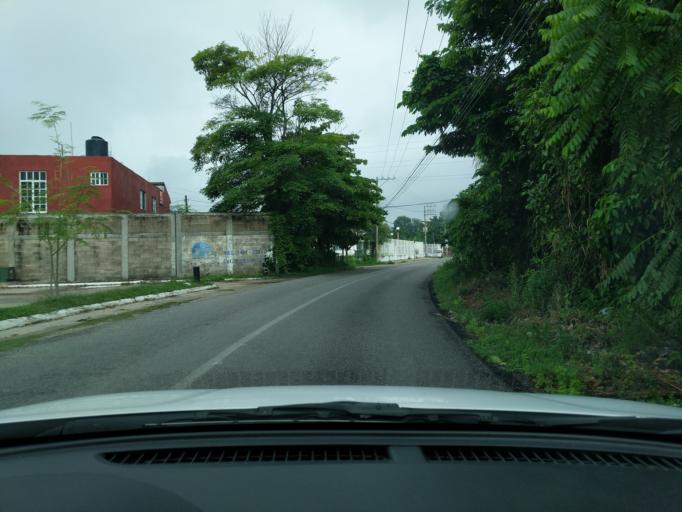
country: MX
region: Tabasco
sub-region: Centro
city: La Lima
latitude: 17.9489
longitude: -92.9642
